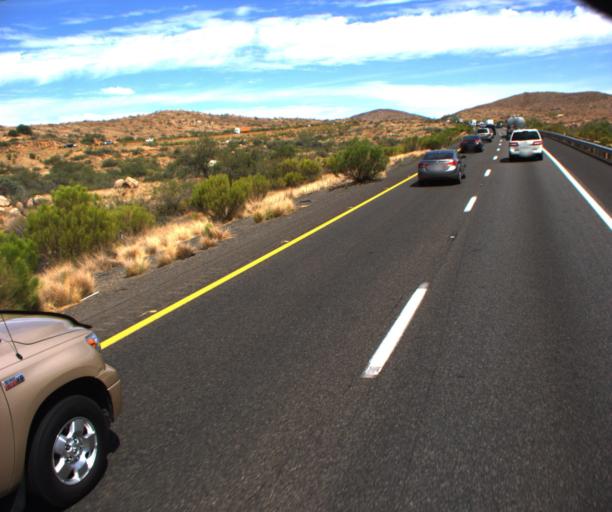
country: US
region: Arizona
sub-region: Yavapai County
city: Cordes Lakes
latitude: 34.2733
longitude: -112.1131
